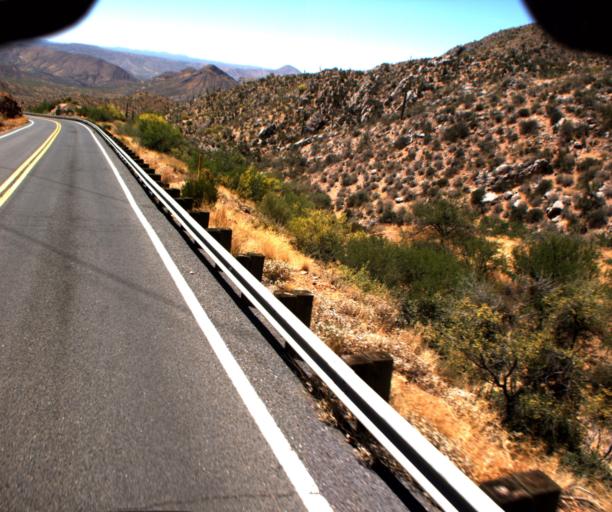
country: US
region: Arizona
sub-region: Pinal County
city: Superior
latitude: 33.1970
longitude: -111.0542
